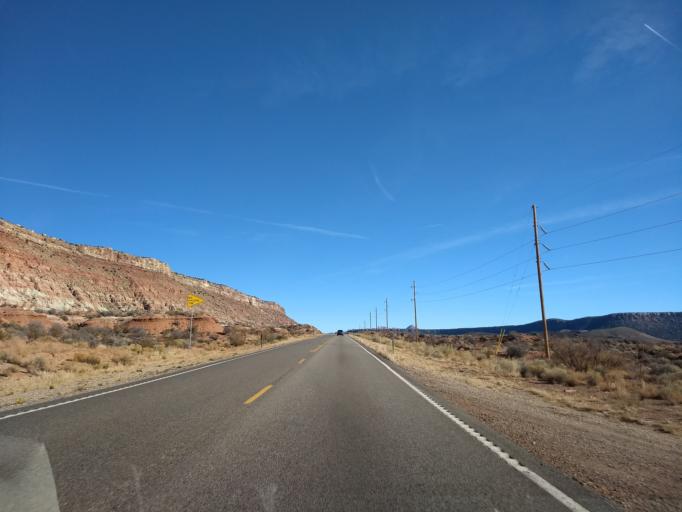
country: US
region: Utah
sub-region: Washington County
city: Hurricane
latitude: 37.1285
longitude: -113.2177
